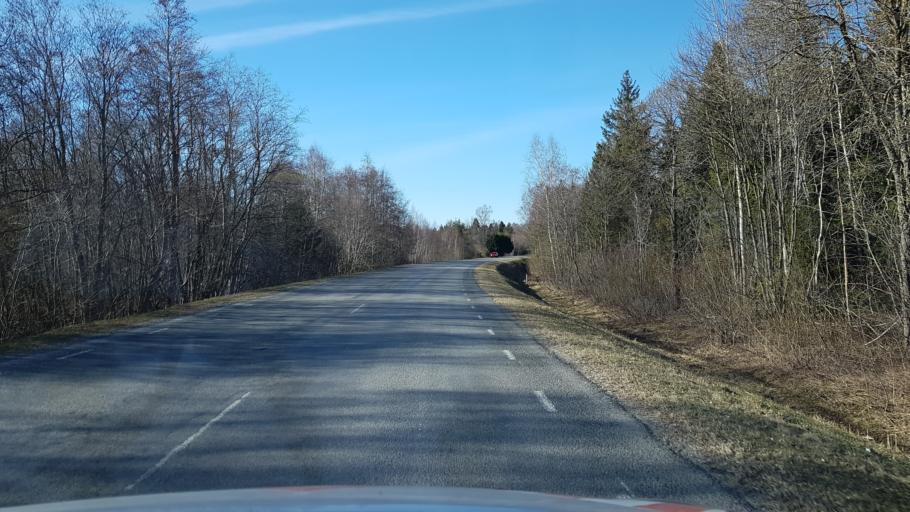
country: EE
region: Harju
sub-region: Keila linn
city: Keila
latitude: 59.2427
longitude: 24.4628
